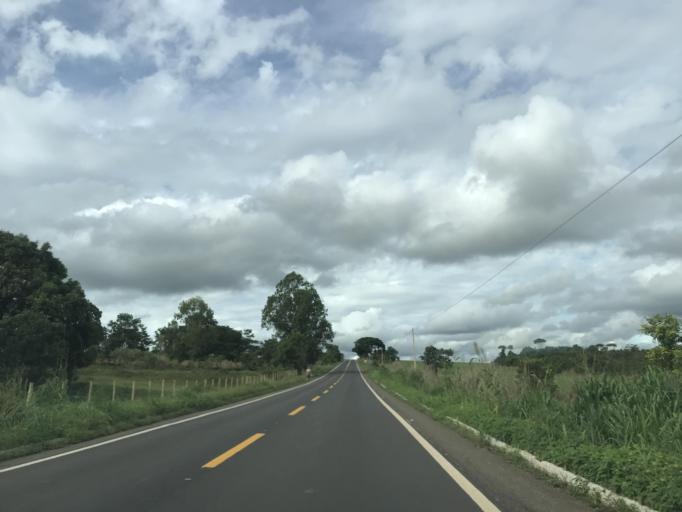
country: BR
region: Goias
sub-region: Piracanjuba
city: Piracanjuba
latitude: -17.1939
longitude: -48.6972
